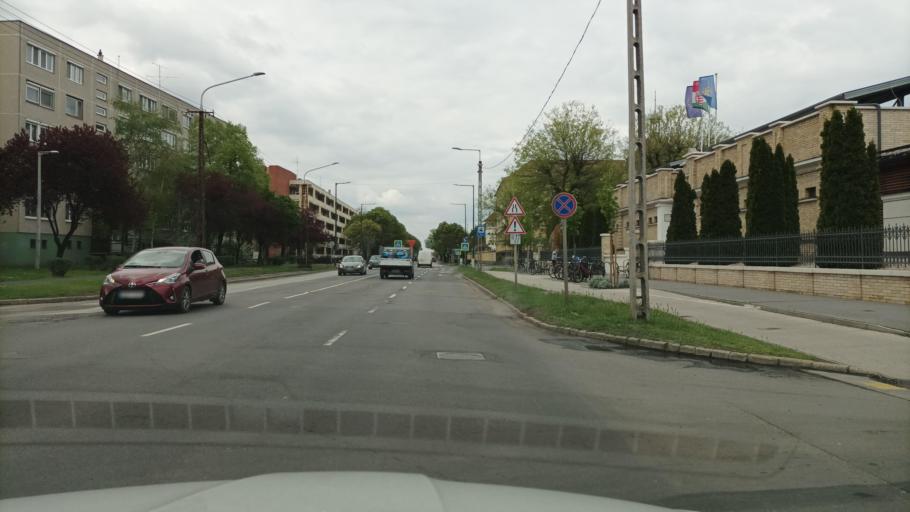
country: HU
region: Pest
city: Cegled
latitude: 47.1757
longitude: 19.8030
